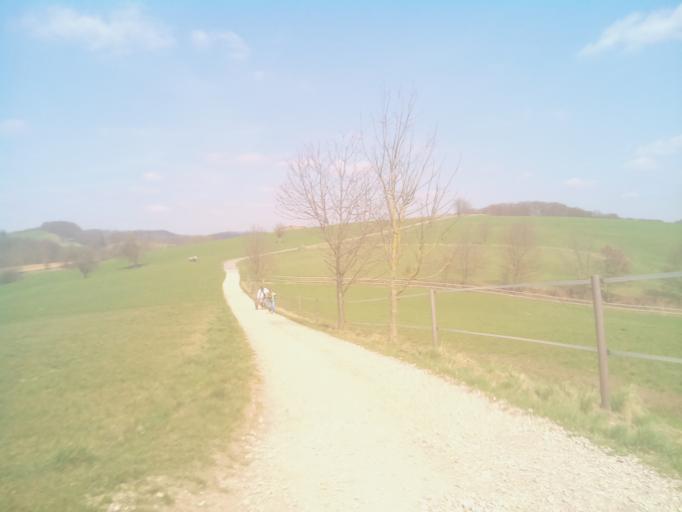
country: DE
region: Hesse
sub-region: Regierungsbezirk Darmstadt
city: Birkenau
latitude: 49.5857
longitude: 8.7104
